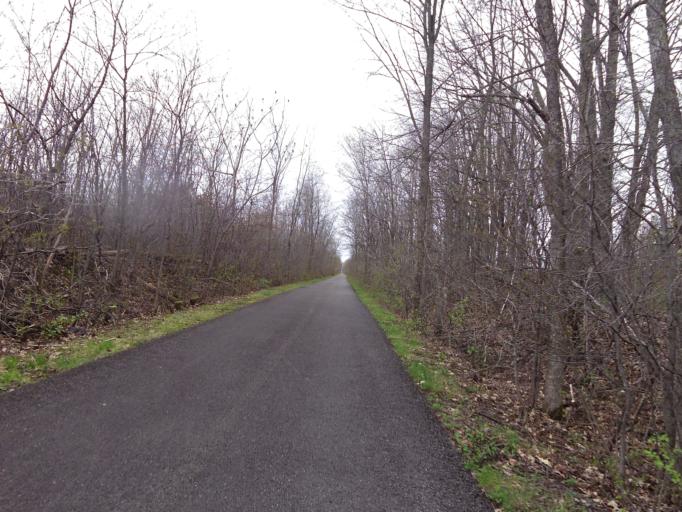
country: CA
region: Quebec
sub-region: Laurentides
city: Brownsburg-Chatham
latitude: 45.5815
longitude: -74.4229
